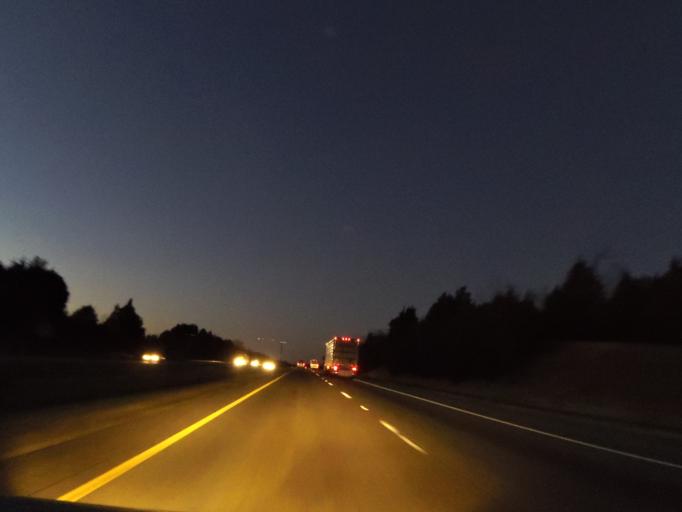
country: US
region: Tennessee
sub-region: Jefferson County
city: White Pine
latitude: 36.0048
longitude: -83.2906
